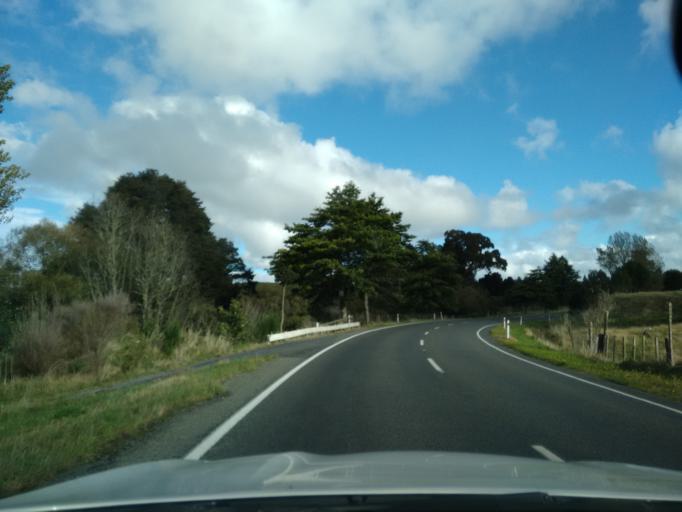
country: NZ
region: Manawatu-Wanganui
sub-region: Ruapehu District
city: Waiouru
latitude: -39.4178
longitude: 175.2844
